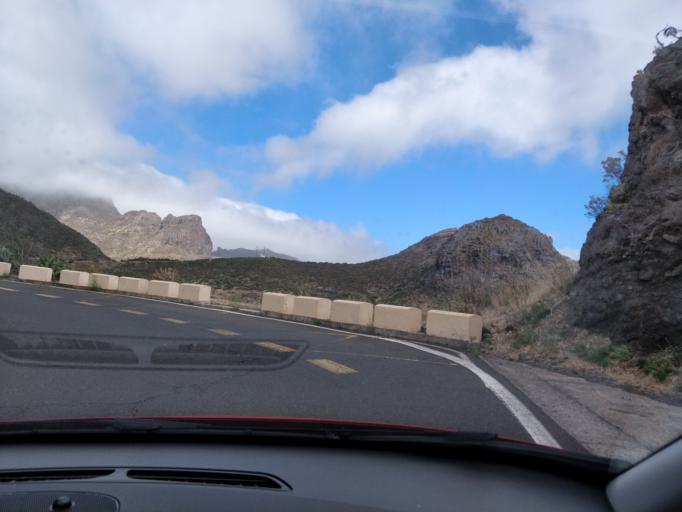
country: ES
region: Canary Islands
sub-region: Provincia de Santa Cruz de Tenerife
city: Santiago del Teide
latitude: 28.3162
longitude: -16.8526
